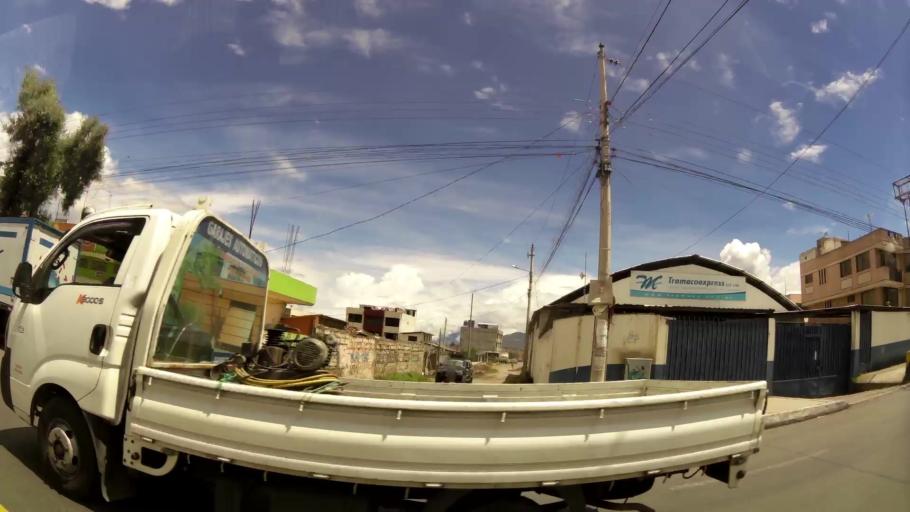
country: EC
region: Tungurahua
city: Ambato
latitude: -1.2769
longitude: -78.6317
